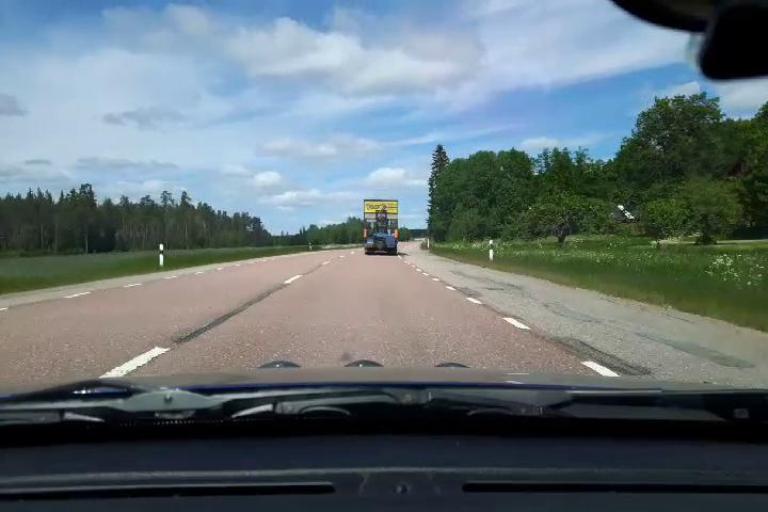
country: SE
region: Uppsala
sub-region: Osthammars Kommun
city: Bjorklinge
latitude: 60.1559
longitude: 17.4911
